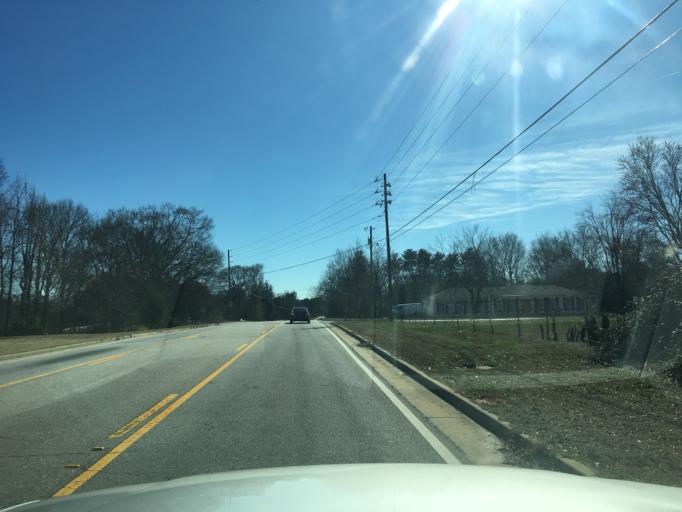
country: US
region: Georgia
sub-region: Rockdale County
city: Conyers
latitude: 33.6597
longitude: -84.0499
